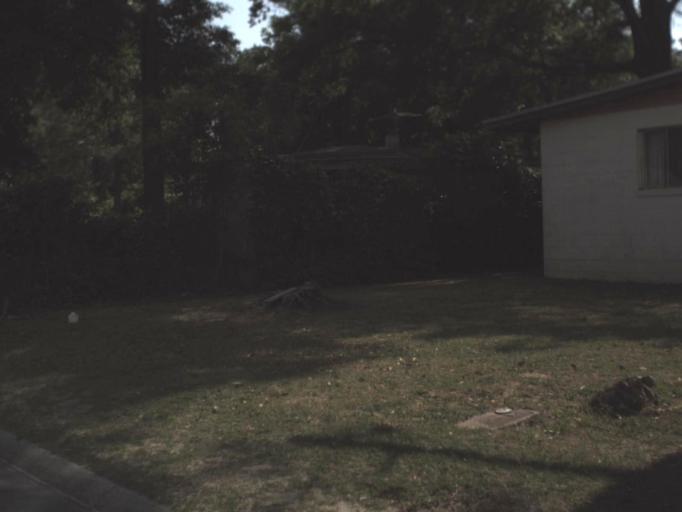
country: US
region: Florida
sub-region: Escambia County
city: Goulding
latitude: 30.4521
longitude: -87.2138
